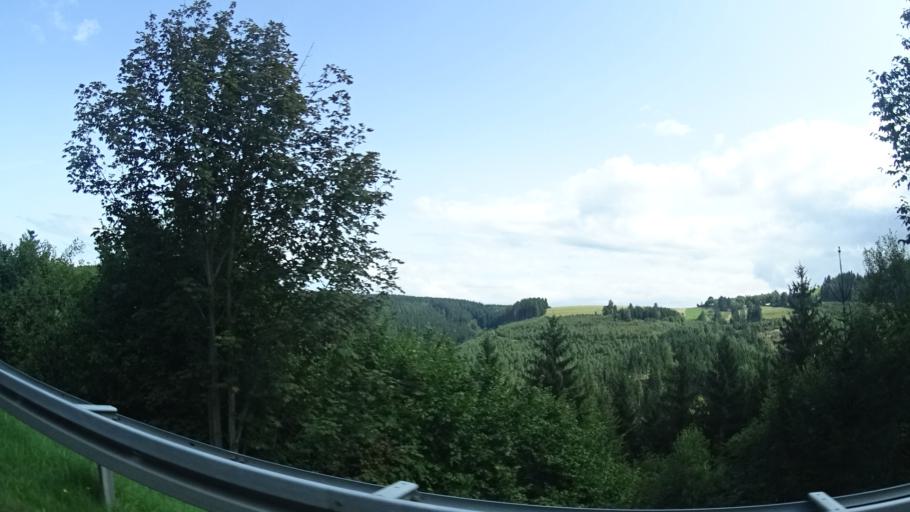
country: DE
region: Thuringia
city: Grafenthal
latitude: 50.5034
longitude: 11.2961
